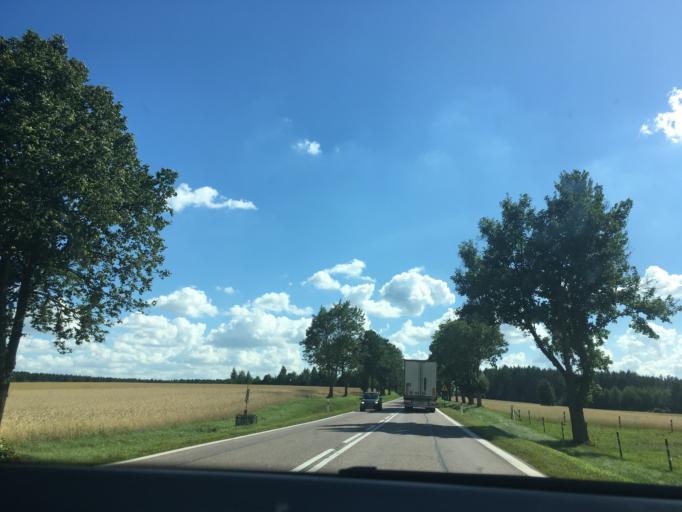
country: PL
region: Podlasie
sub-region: Powiat sokolski
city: Suchowola
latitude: 53.6091
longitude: 23.1176
